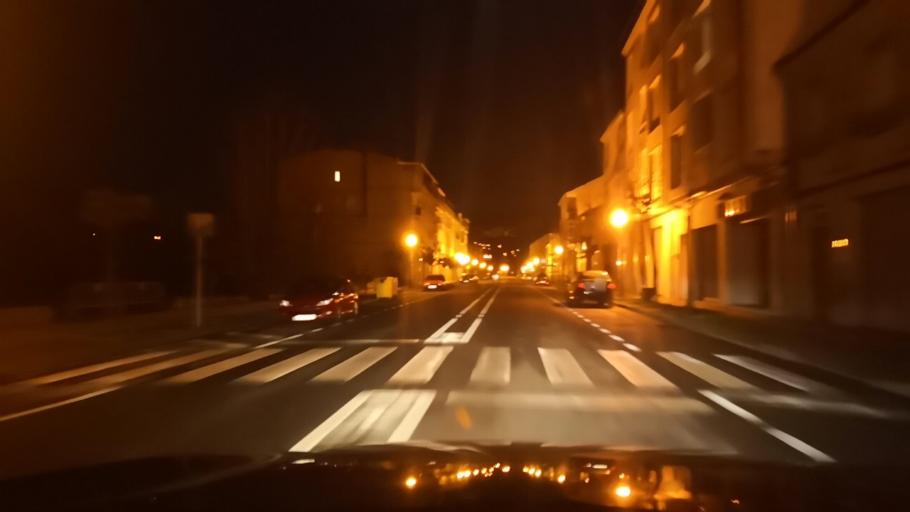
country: ES
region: Galicia
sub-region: Provincia de Ourense
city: Verin
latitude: 41.9402
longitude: -7.4268
